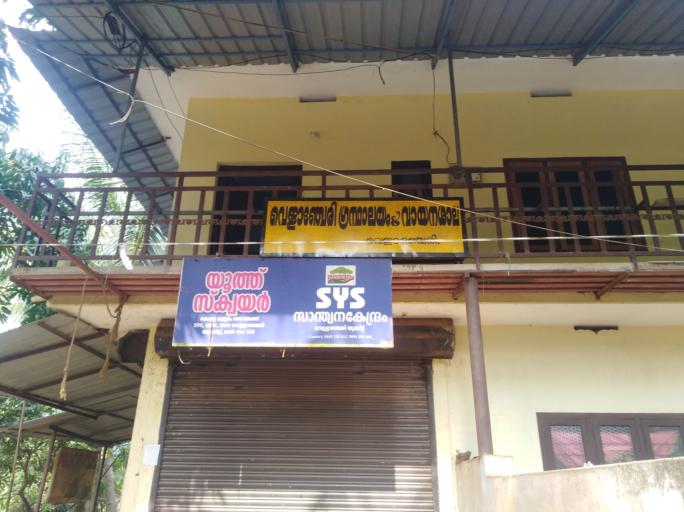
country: IN
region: Kerala
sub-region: Malappuram
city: Tirur
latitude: 10.8546
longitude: 76.0065
